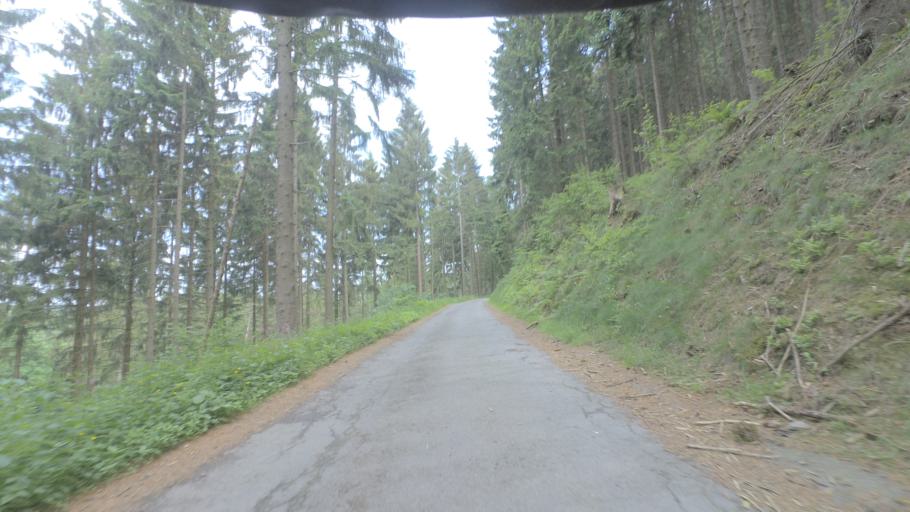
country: DE
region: Lower Saxony
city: Goslar
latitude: 51.8977
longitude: 10.4527
